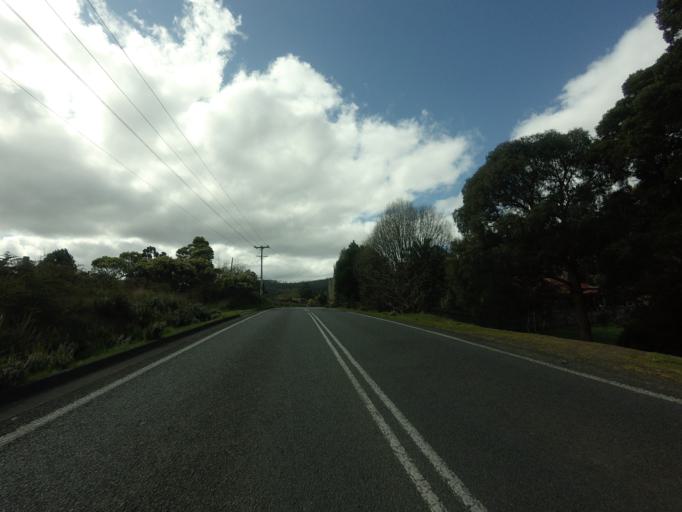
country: AU
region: Tasmania
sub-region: Huon Valley
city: Geeveston
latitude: -43.3004
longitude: 147.0079
